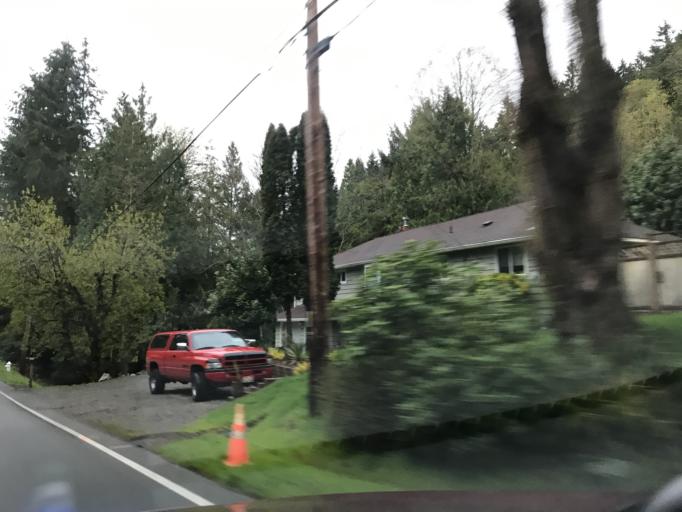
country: US
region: Washington
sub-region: Snohomish County
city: Brier
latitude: 47.7734
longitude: -122.2889
